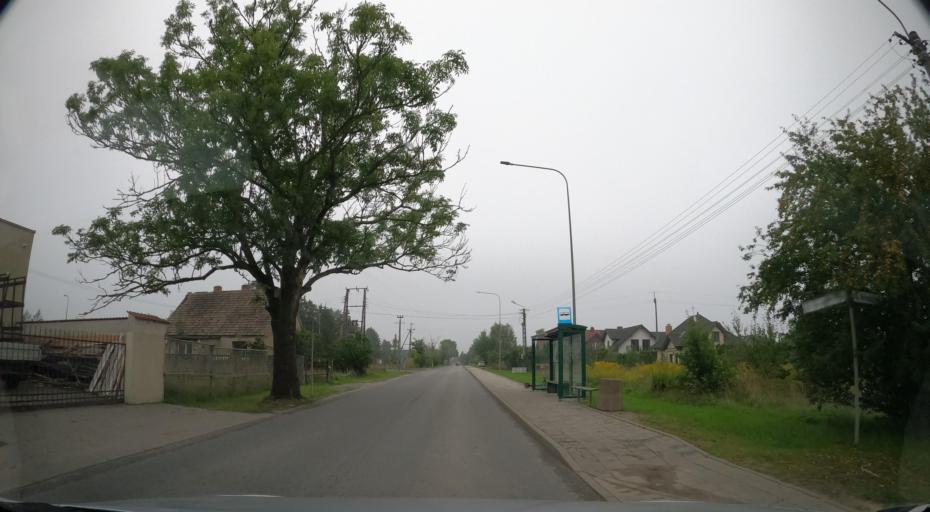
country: PL
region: Pomeranian Voivodeship
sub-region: Powiat kartuski
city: Chwaszczyno
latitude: 54.4213
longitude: 18.4535
